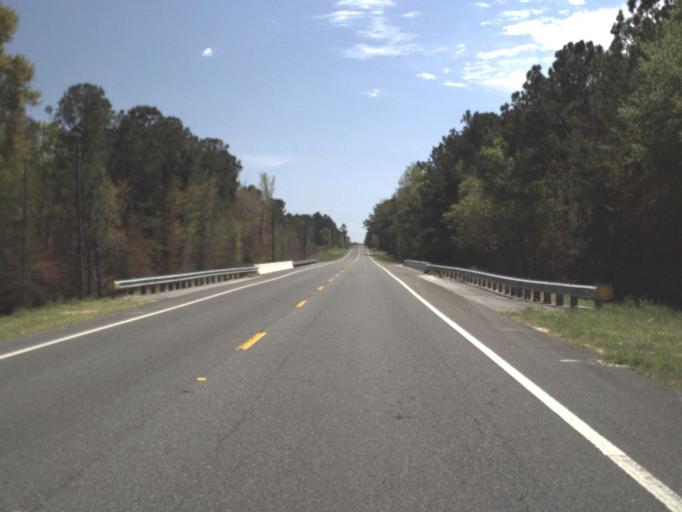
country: US
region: Alabama
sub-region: Geneva County
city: Geneva
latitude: 30.8995
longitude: -85.9549
